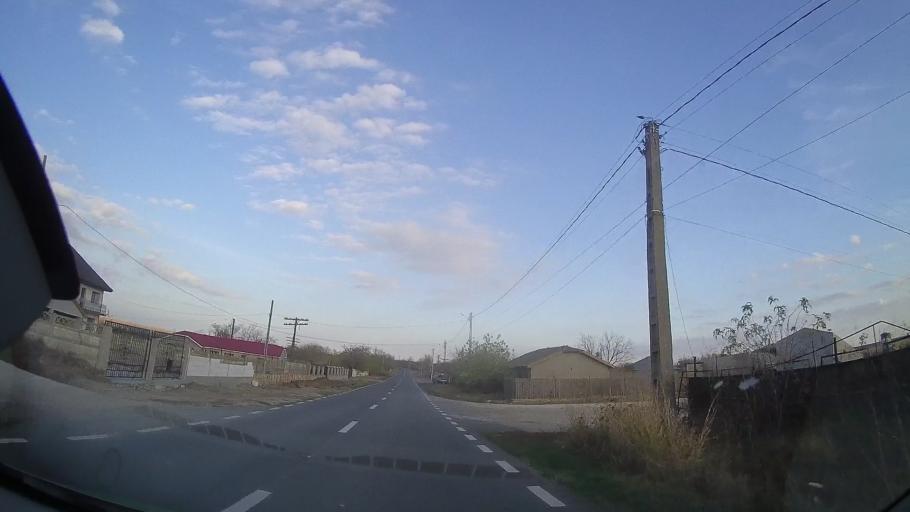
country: RO
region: Constanta
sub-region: Comuna Chirnogeni
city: Plopeni
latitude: 43.9508
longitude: 28.1821
